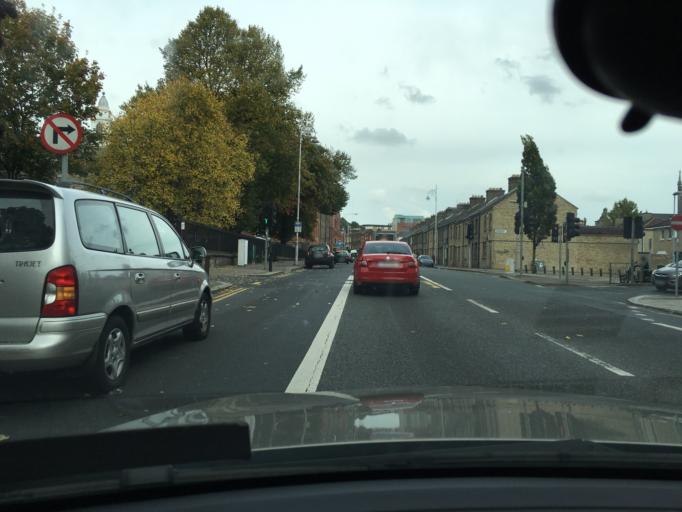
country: IE
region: Leinster
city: Rialto
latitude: 53.3484
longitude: -6.2821
